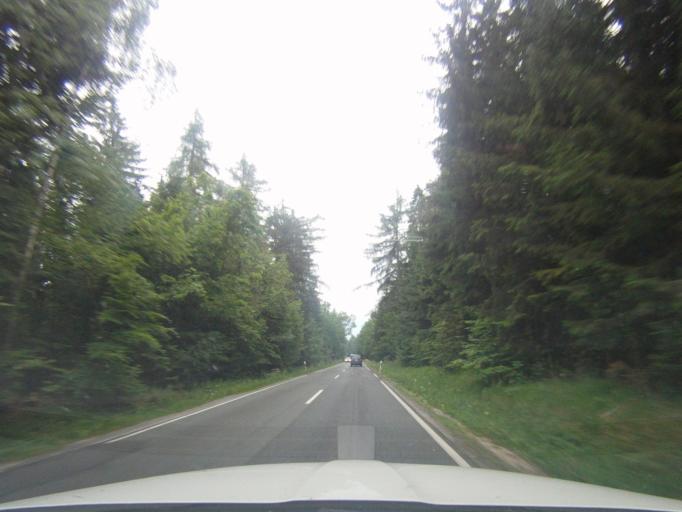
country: DE
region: Thuringia
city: Veilsdorf
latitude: 50.4821
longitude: 10.8396
